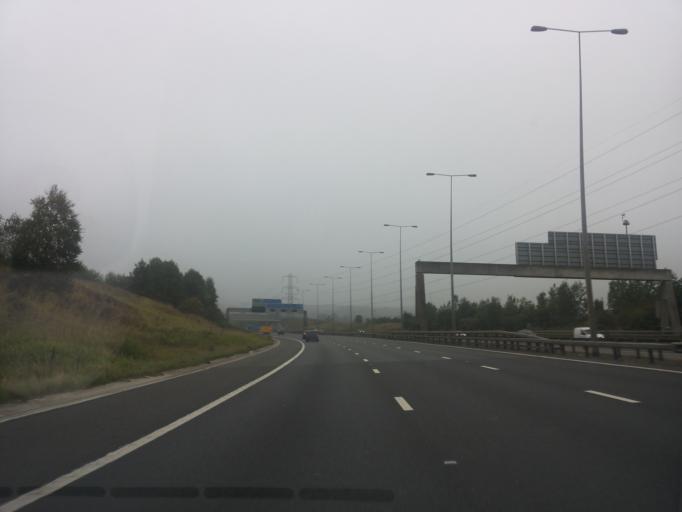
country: GB
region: England
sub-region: Borough of Rochdale
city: Middleton
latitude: 53.5412
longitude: -2.2209
